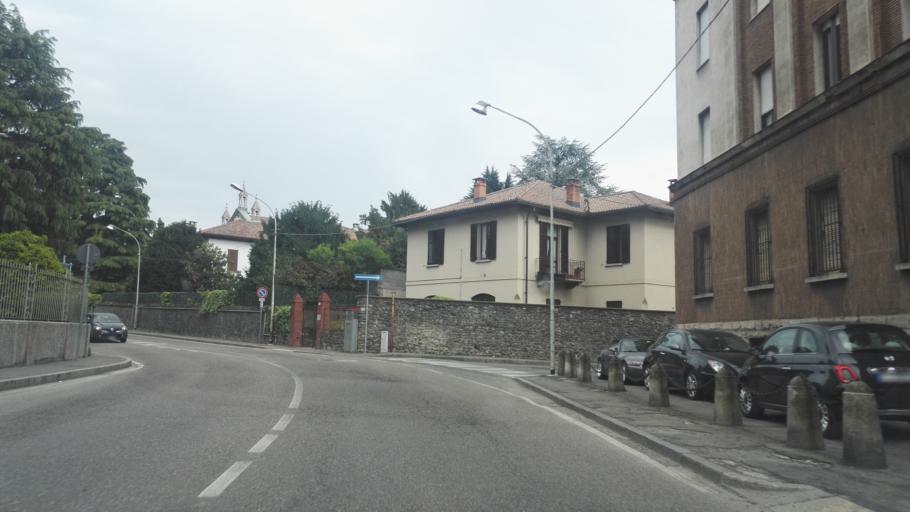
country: IT
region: Lombardy
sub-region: Provincia di Como
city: Brunate
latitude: 45.8063
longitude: 9.0954
